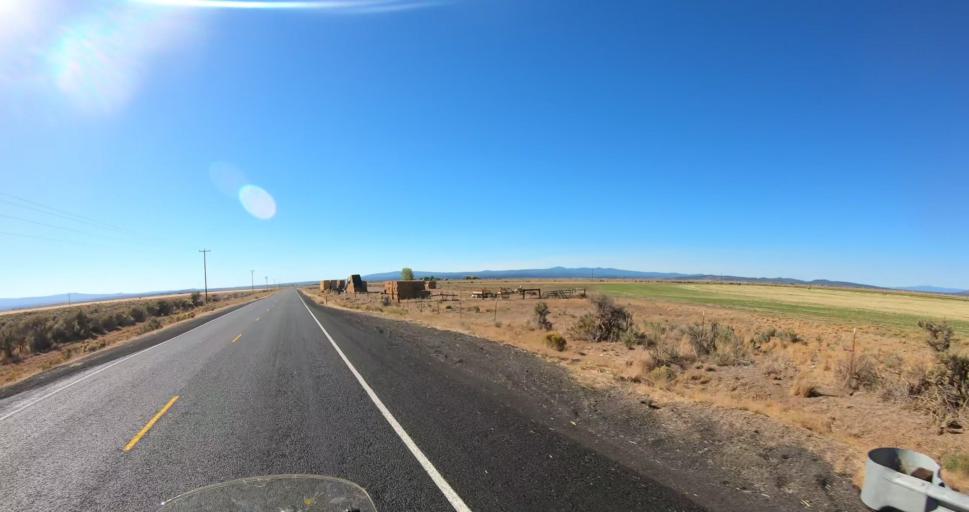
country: US
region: Oregon
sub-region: Deschutes County
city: La Pine
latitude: 43.1279
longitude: -120.9833
